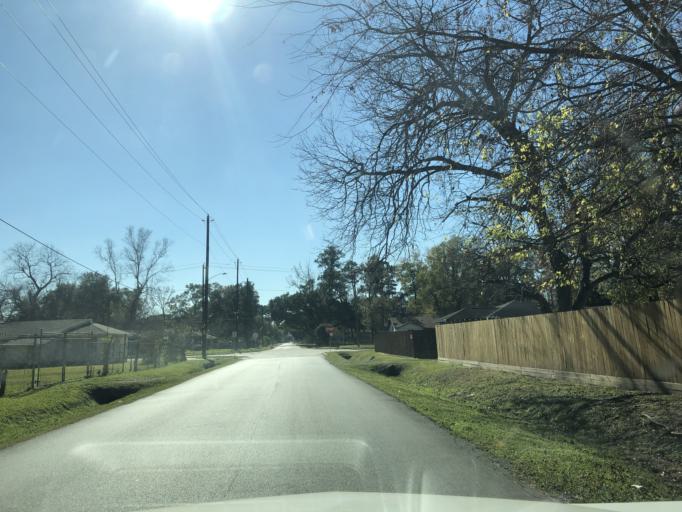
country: US
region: Texas
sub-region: Harris County
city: Jacinto City
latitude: 29.8322
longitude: -95.2938
